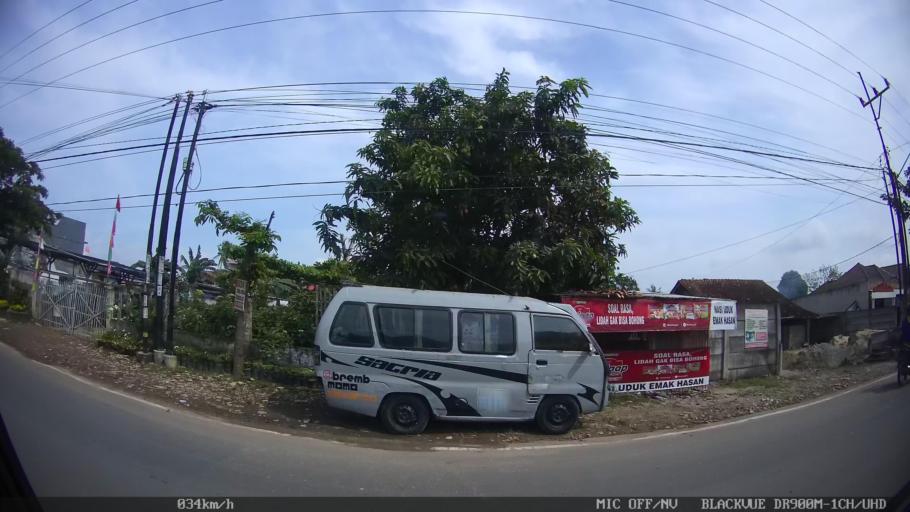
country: ID
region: Lampung
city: Kedaton
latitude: -5.3830
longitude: 105.2974
